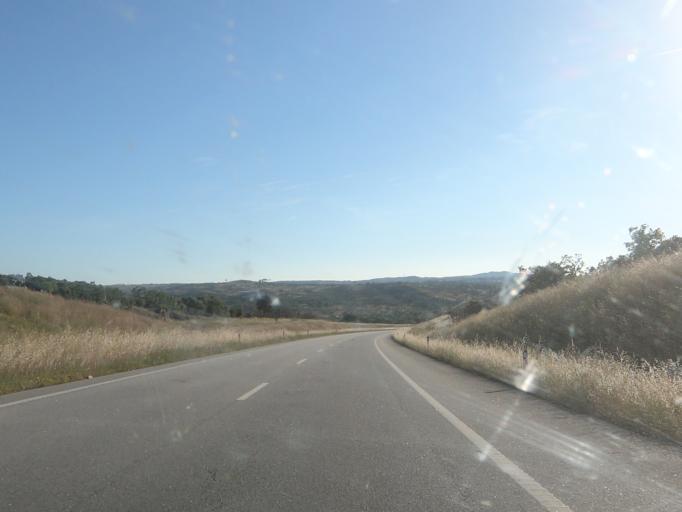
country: PT
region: Guarda
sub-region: Pinhel
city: Pinhel
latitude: 40.6057
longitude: -7.0180
